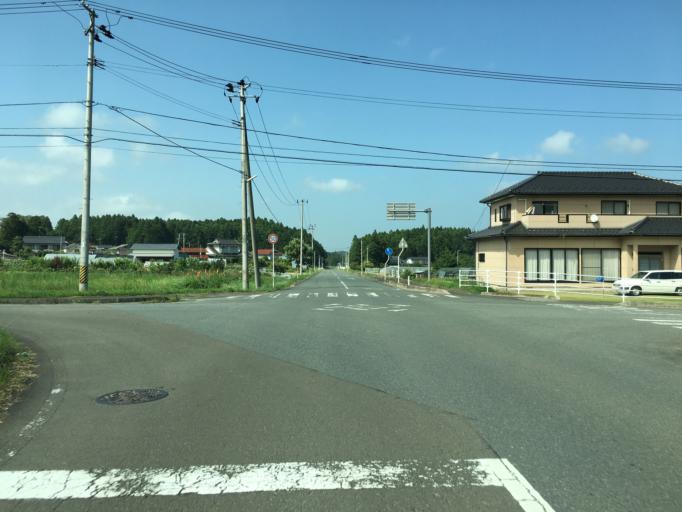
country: JP
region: Miyagi
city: Marumori
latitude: 37.8800
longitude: 140.8890
